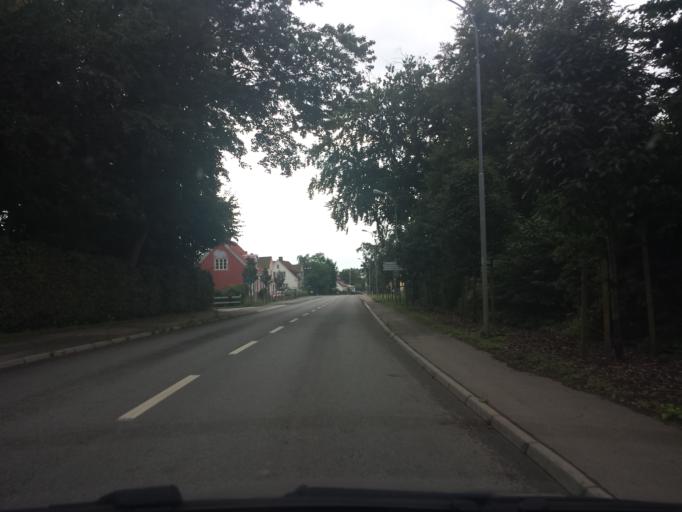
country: SE
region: Skane
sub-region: Ystads Kommun
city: Kopingebro
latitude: 55.4532
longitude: 14.0202
